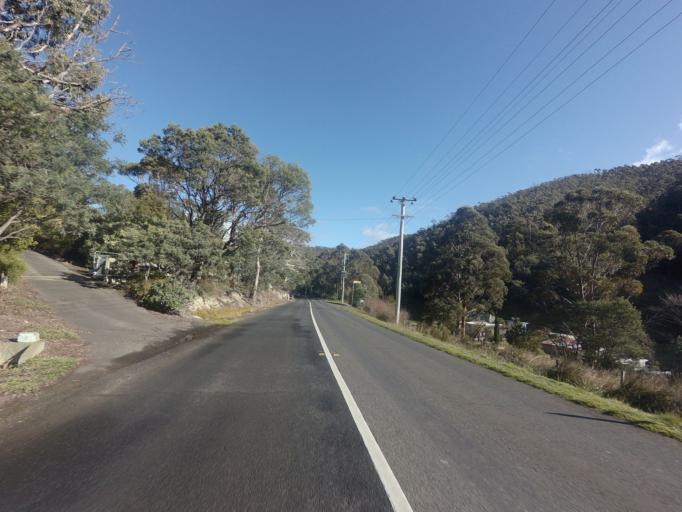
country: AU
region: Tasmania
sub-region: Glenorchy
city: Berriedale
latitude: -42.8180
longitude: 147.2222
